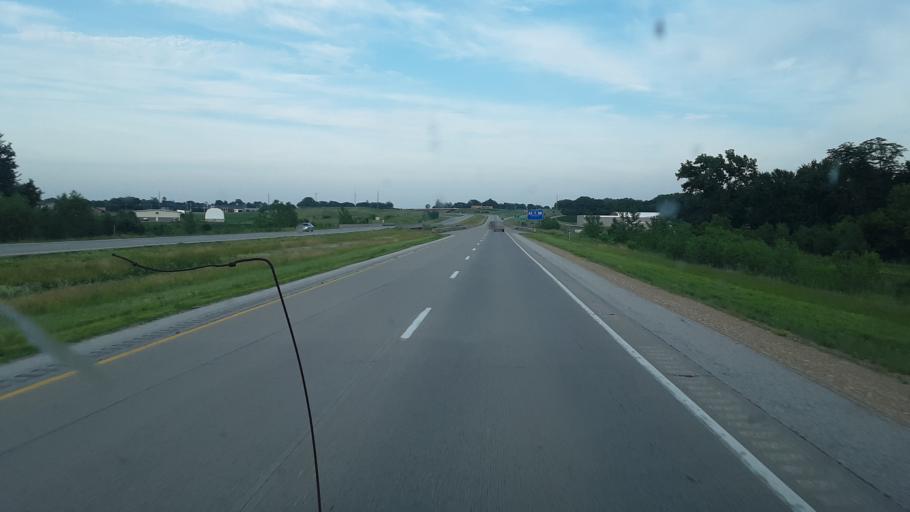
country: US
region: Iowa
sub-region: Tama County
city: Toledo
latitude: 41.9841
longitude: -92.5969
